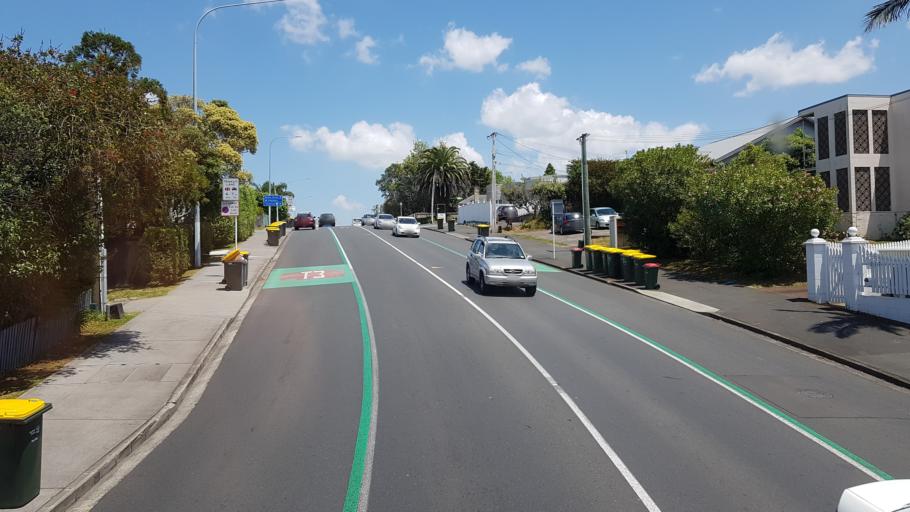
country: NZ
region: Auckland
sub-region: Auckland
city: North Shore
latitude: -36.8101
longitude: 174.7282
